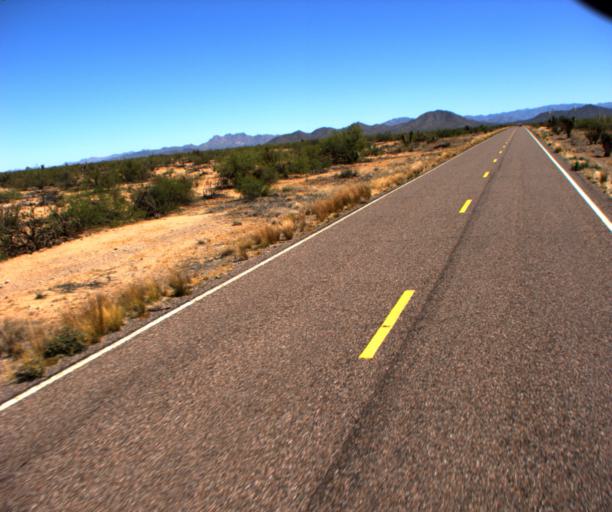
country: US
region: Arizona
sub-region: Yavapai County
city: Congress
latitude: 34.0532
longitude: -113.0549
